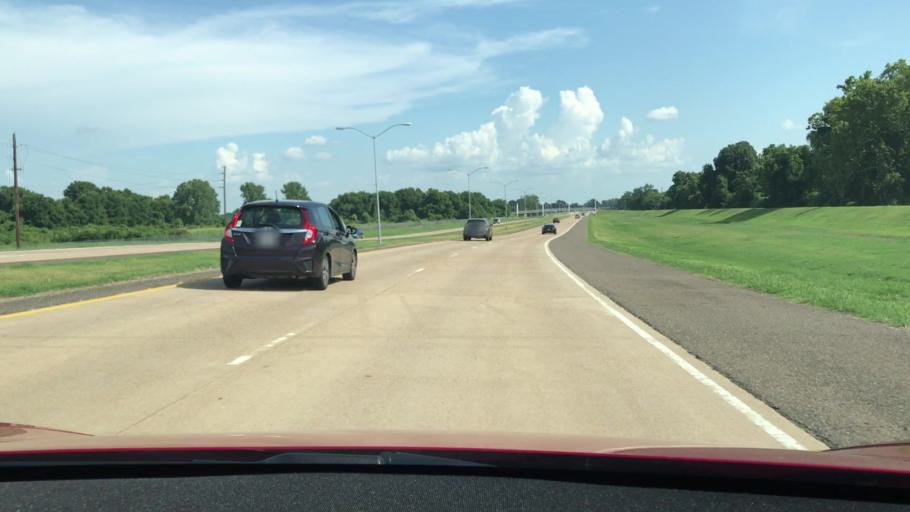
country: US
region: Louisiana
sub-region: Bossier Parish
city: Bossier City
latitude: 32.4760
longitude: -93.6794
